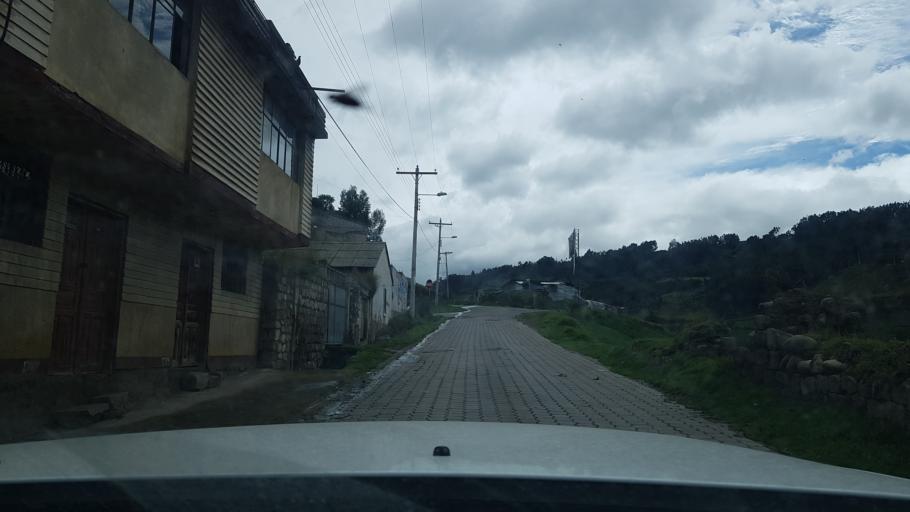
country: EC
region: Chimborazo
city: Riobamba
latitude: -1.7038
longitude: -78.7774
